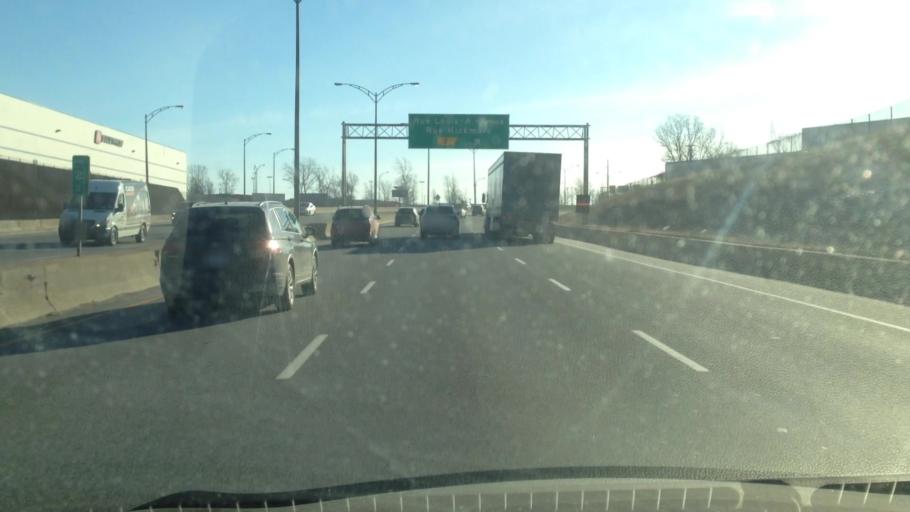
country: CA
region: Quebec
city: Cote-Saint-Luc
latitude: 45.4673
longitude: -73.6984
